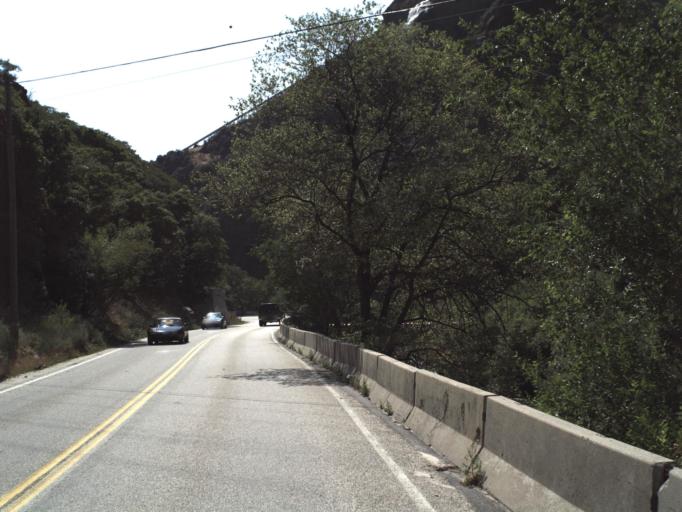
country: US
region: Utah
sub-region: Weber County
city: Ogden
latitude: 41.2370
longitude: -111.9176
